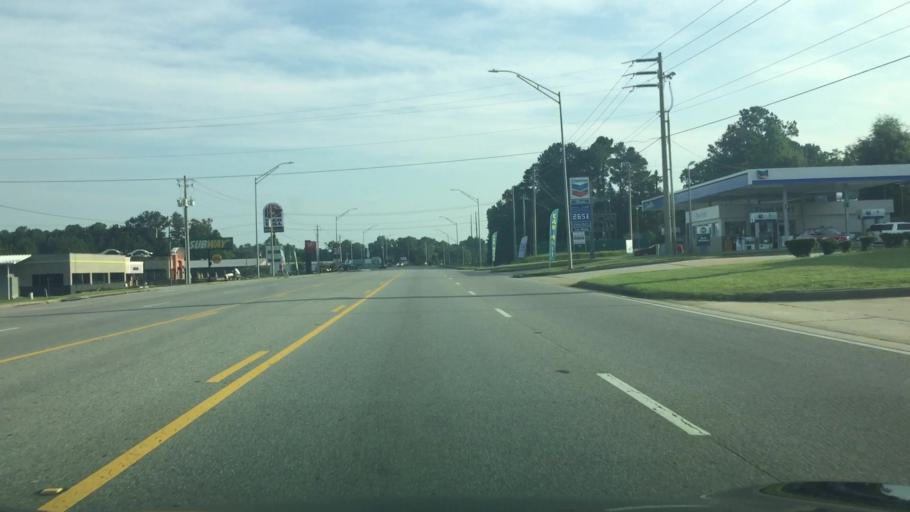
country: US
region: Alabama
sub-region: Covington County
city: Andalusia
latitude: 31.3092
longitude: -86.4994
